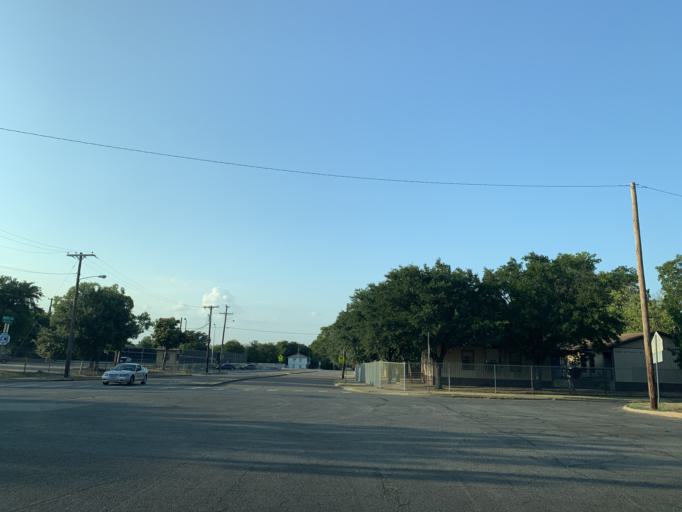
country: US
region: Texas
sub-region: Dallas County
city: Cockrell Hill
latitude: 32.7451
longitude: -96.8527
